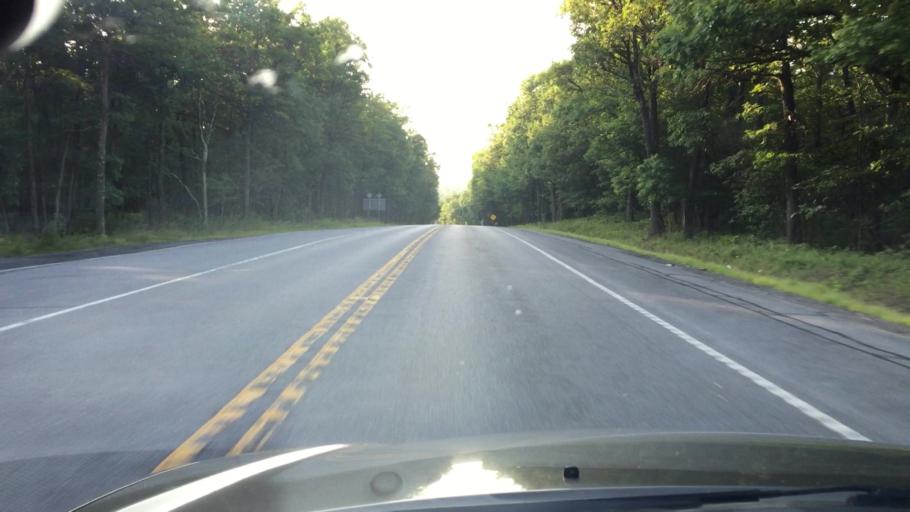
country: US
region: Pennsylvania
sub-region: Carbon County
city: Nesquehoning
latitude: 40.8890
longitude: -75.8037
